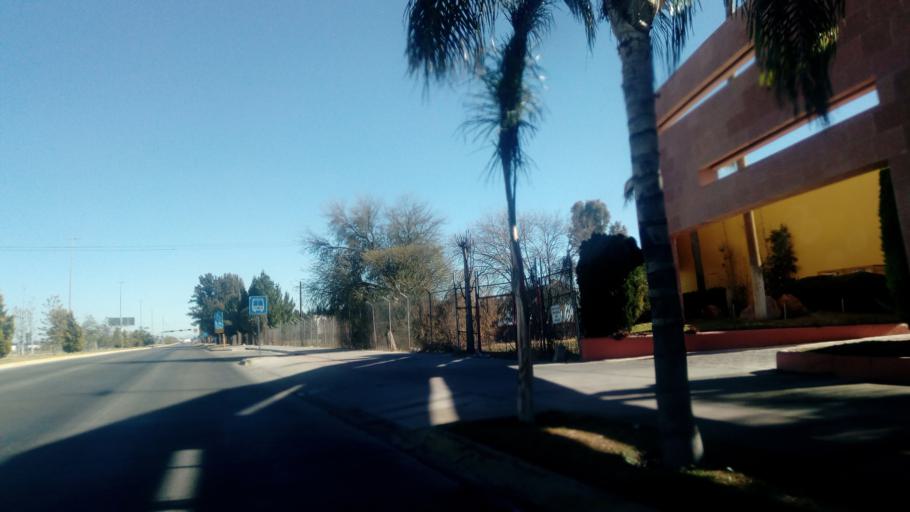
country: MX
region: Durango
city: Victoria de Durango
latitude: 24.0788
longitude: -104.5892
